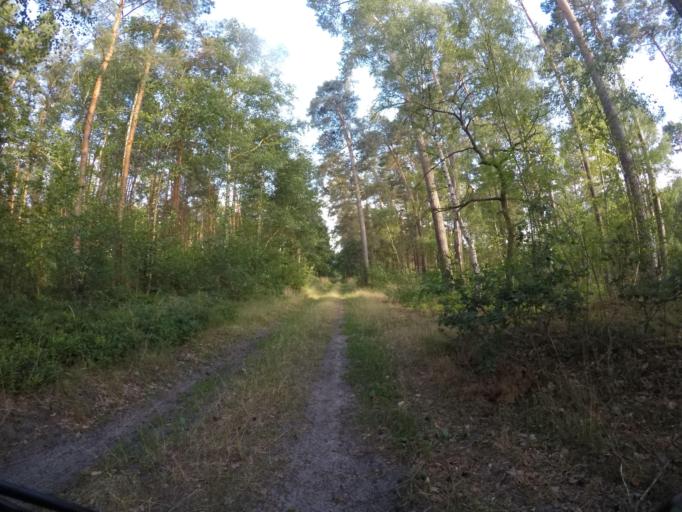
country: DE
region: Lower Saxony
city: Hitzacker
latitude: 53.2316
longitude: 11.0456
